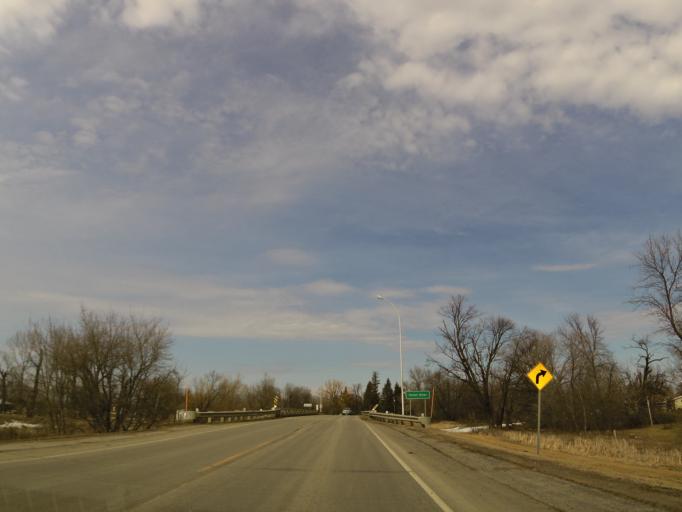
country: US
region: North Dakota
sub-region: Walsh County
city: Grafton
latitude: 48.2840
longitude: -97.3703
